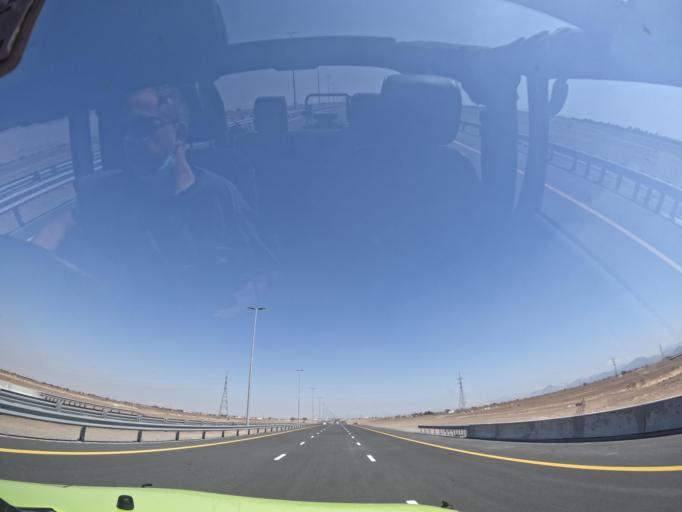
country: AE
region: Ash Shariqah
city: Adh Dhayd
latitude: 25.0996
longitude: 55.9272
